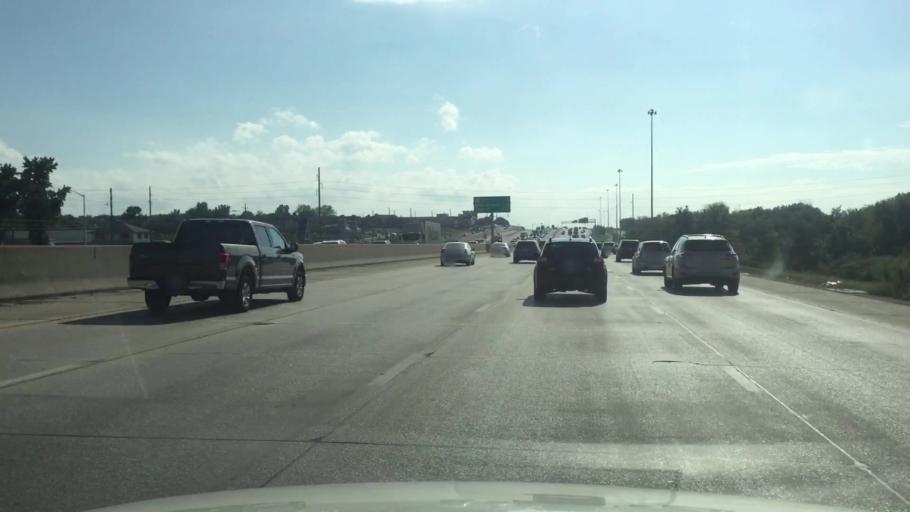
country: US
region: Kansas
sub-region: Johnson County
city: Overland Park
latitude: 38.9890
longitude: -94.7020
